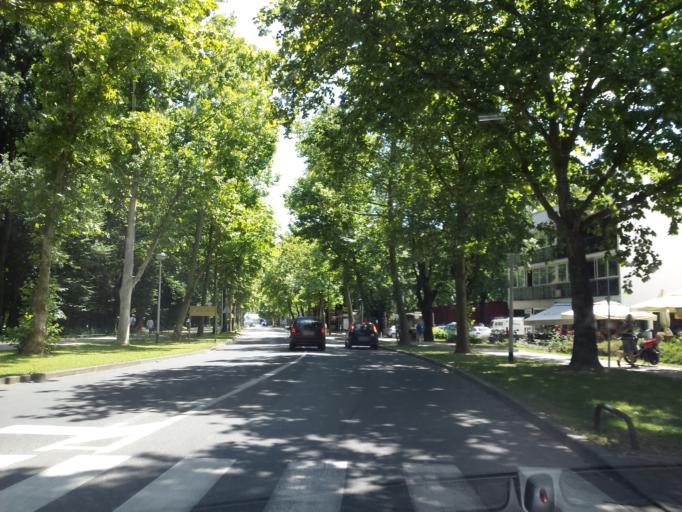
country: HR
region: Grad Zagreb
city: Zagreb
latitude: 45.8225
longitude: 16.0123
